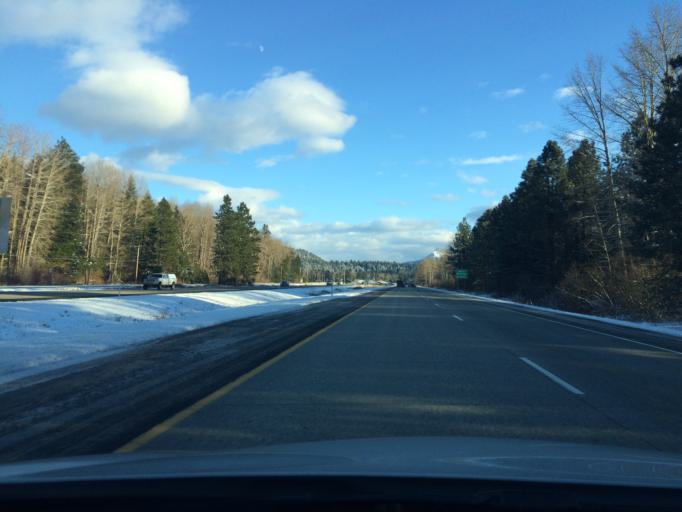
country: US
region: Washington
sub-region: Kittitas County
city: Cle Elum
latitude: 47.1986
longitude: -121.0646
